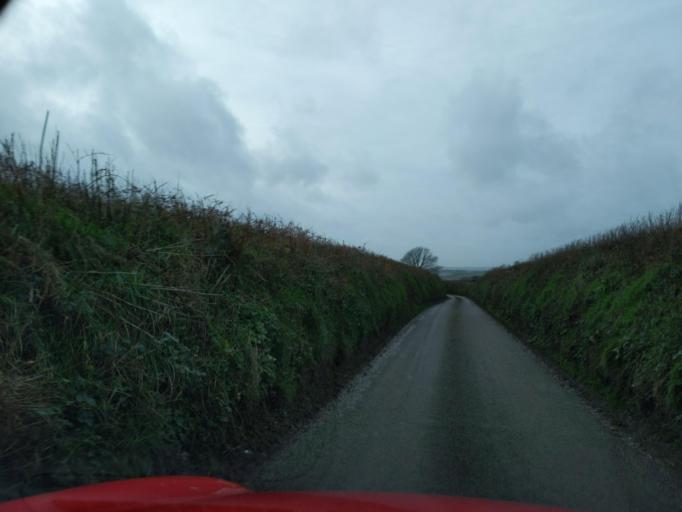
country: GB
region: England
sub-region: Cornwall
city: Fowey
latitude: 50.3429
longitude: -4.5693
